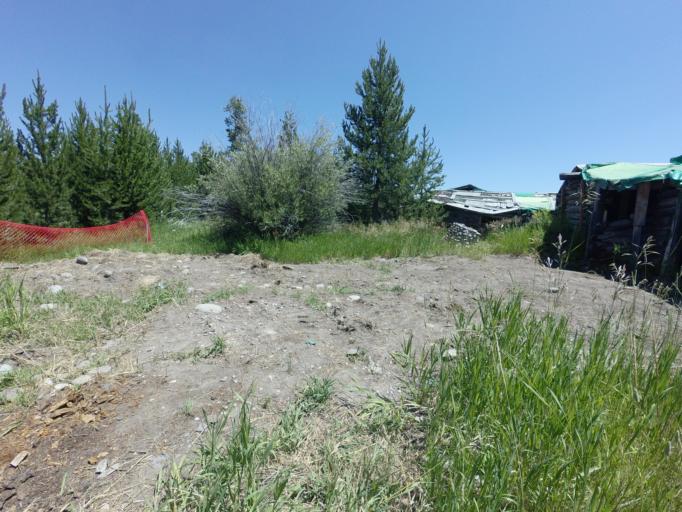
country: US
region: Wyoming
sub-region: Teton County
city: Jackson
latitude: 43.6950
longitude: -110.6957
